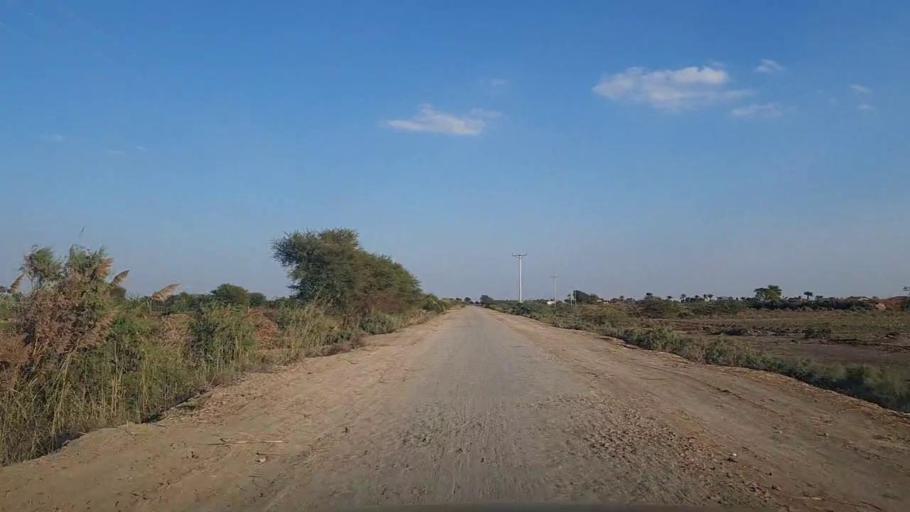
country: PK
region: Sindh
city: Jhol
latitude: 25.9252
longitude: 69.0187
